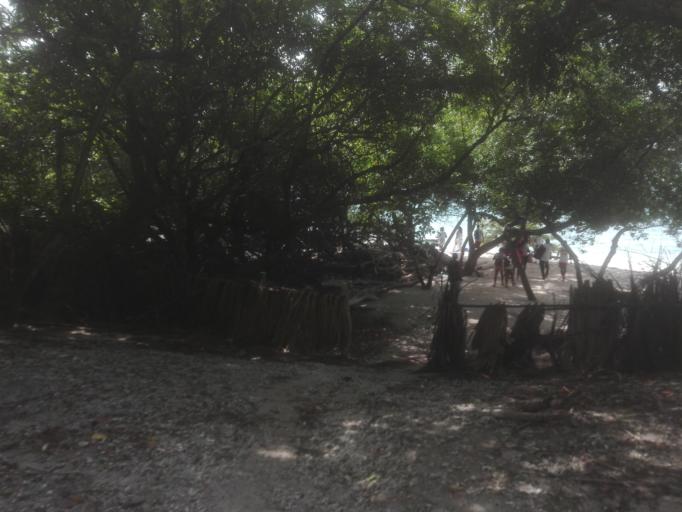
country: CO
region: Bolivar
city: Turbana
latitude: 10.1809
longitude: -75.7317
